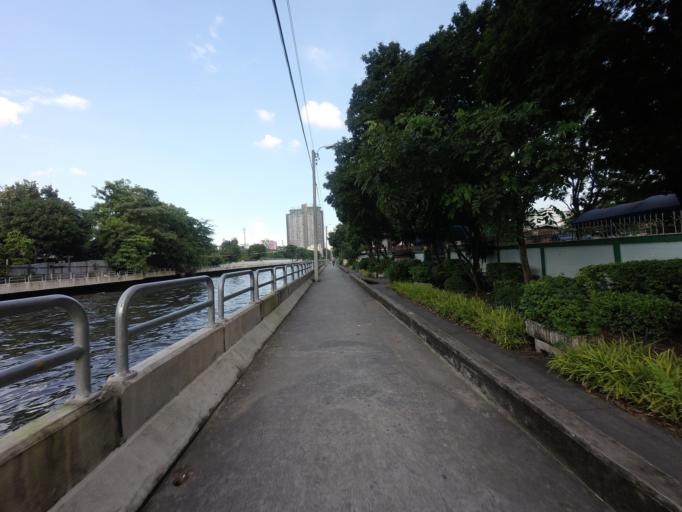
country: TH
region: Bangkok
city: Watthana
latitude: 13.7445
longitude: 100.5798
